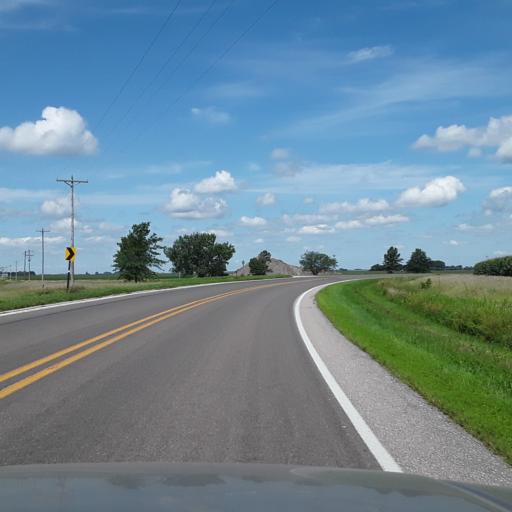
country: US
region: Nebraska
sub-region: Polk County
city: Osceola
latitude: 41.0760
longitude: -97.4222
